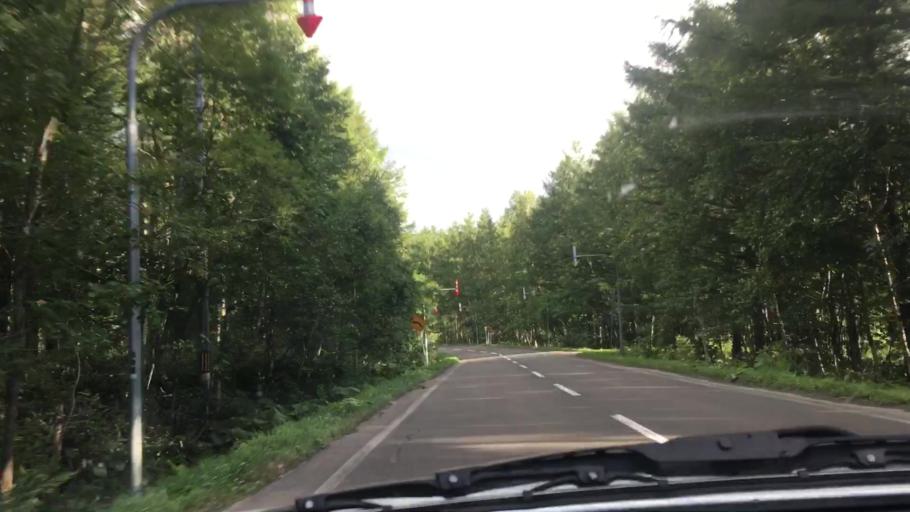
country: JP
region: Hokkaido
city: Shimo-furano
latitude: 43.1167
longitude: 142.6828
